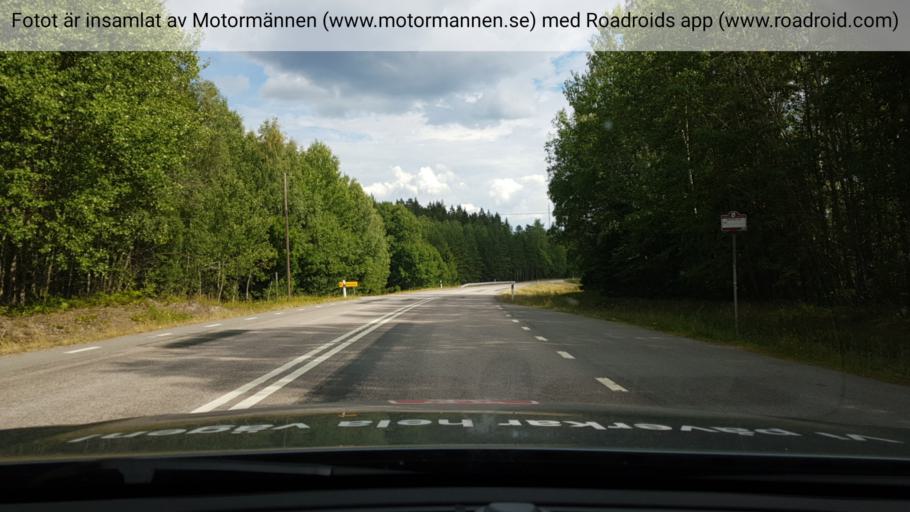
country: SE
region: Uppsala
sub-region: Heby Kommun
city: Morgongava
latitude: 59.9176
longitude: 17.0211
